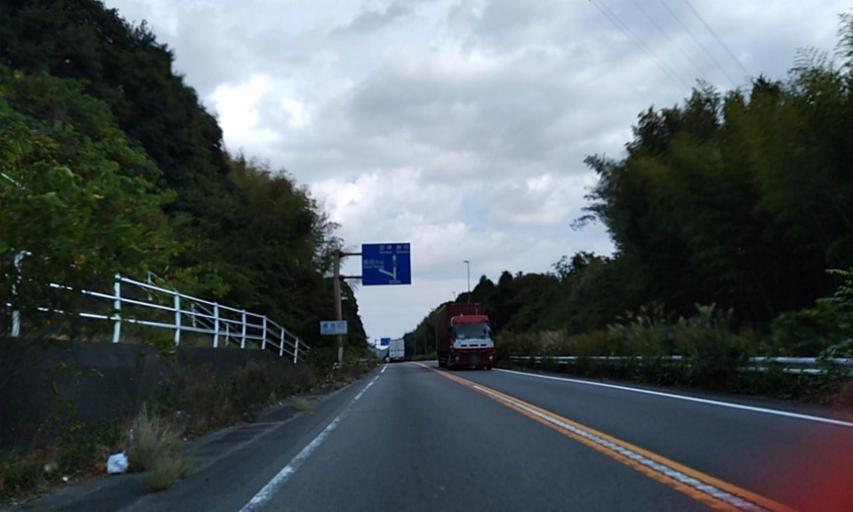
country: JP
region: Shizuoka
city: Shimada
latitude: 34.8460
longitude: 138.1612
